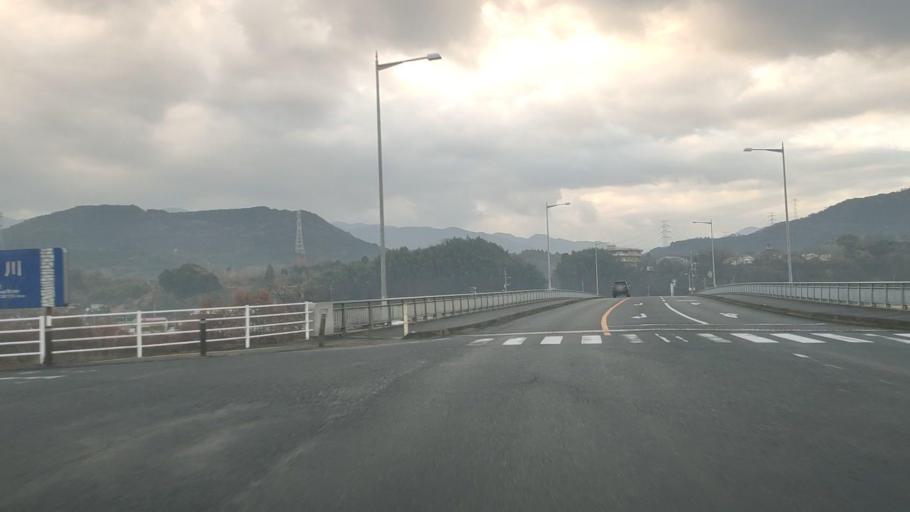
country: JP
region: Kumamoto
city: Matsubase
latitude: 32.6430
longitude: 130.8130
